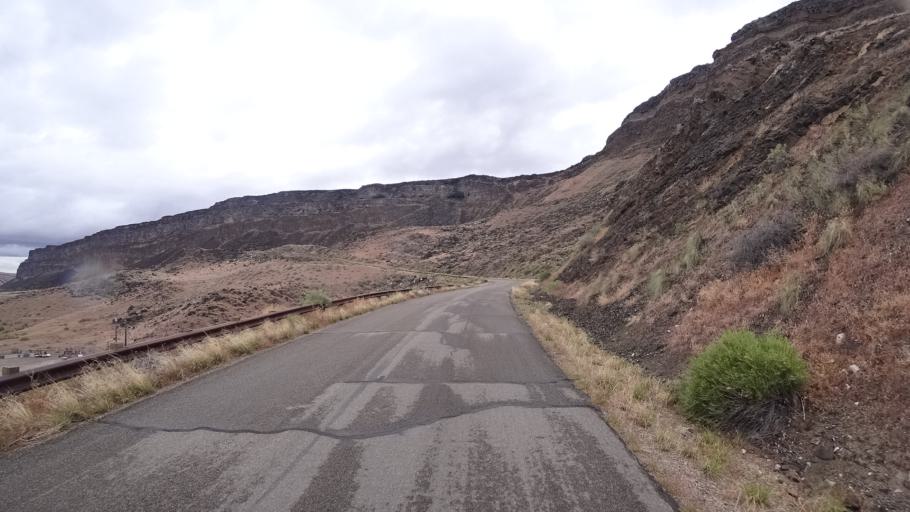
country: US
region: Idaho
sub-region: Owyhee County
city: Murphy
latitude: 43.2457
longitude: -116.3765
